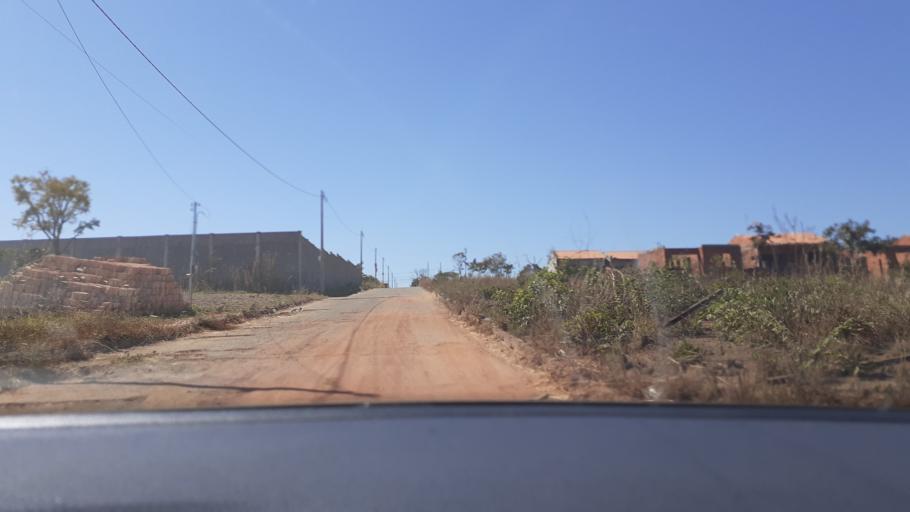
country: BR
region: Goias
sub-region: Aparecida De Goiania
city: Aparecida de Goiania
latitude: -16.8804
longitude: -49.2599
